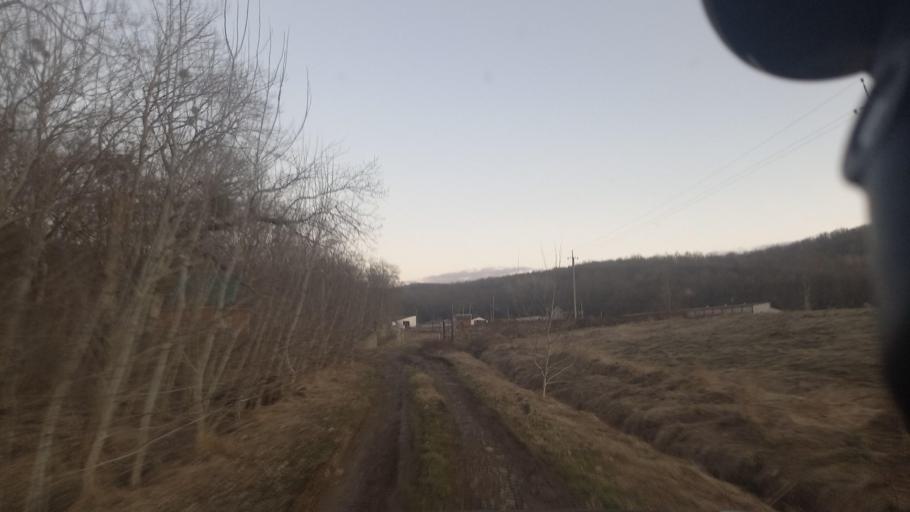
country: RU
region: Krasnodarskiy
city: Smolenskaya
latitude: 44.7261
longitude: 38.8417
